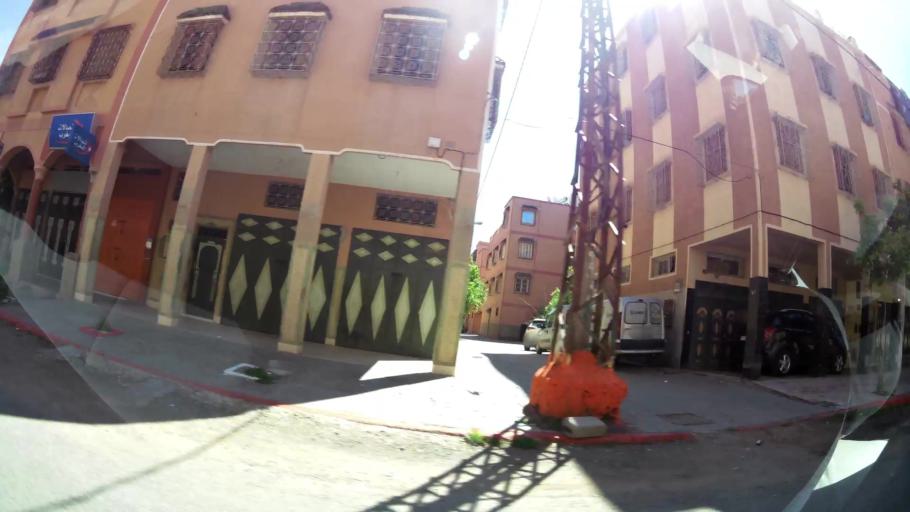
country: MA
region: Marrakech-Tensift-Al Haouz
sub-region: Marrakech
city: Marrakesh
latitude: 31.6324
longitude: -8.0696
